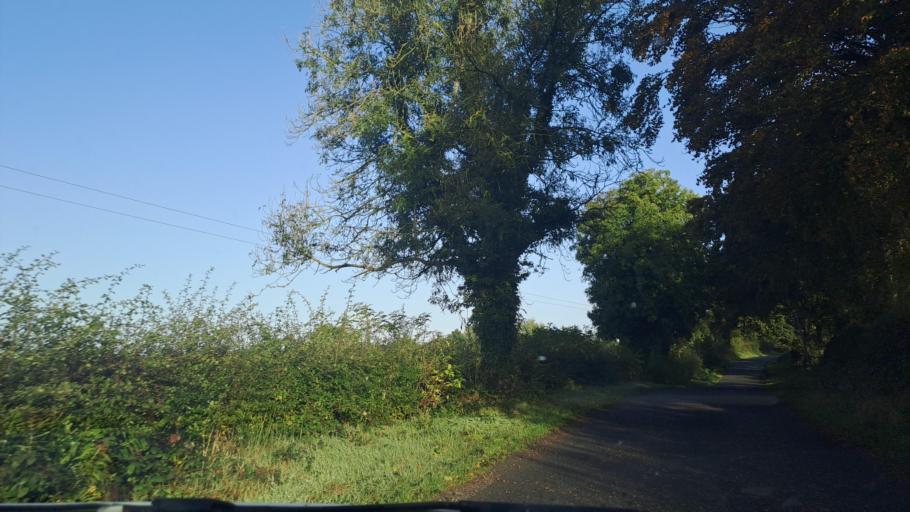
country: IE
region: Ulster
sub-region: County Monaghan
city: Castleblayney
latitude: 54.0449
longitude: -6.8509
